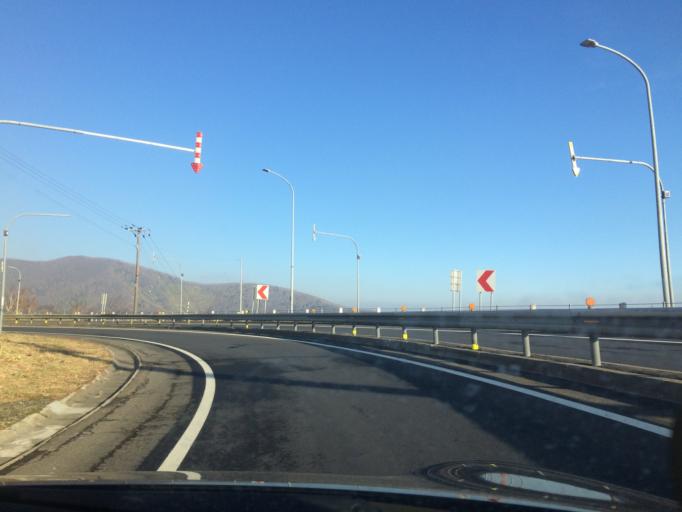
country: JP
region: Hokkaido
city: Otofuke
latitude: 42.9694
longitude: 142.7986
